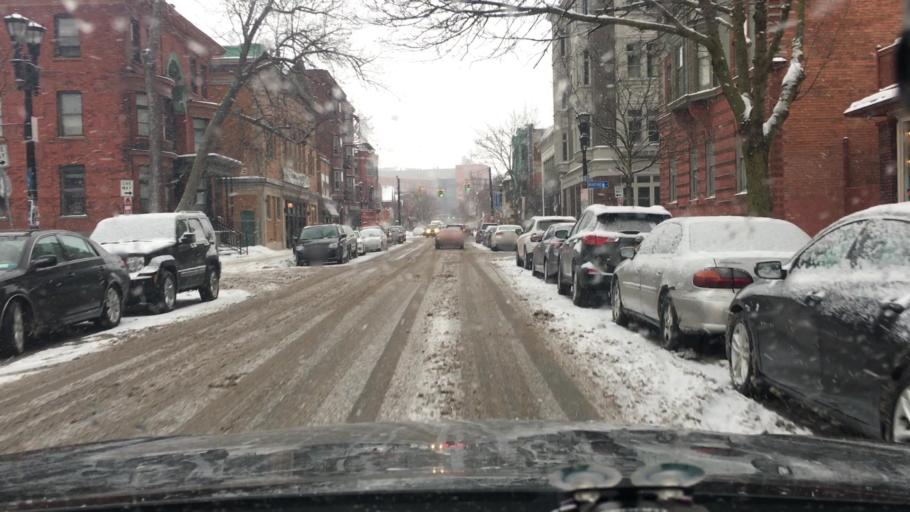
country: US
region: New York
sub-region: Erie County
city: Buffalo
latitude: 42.8995
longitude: -78.8785
